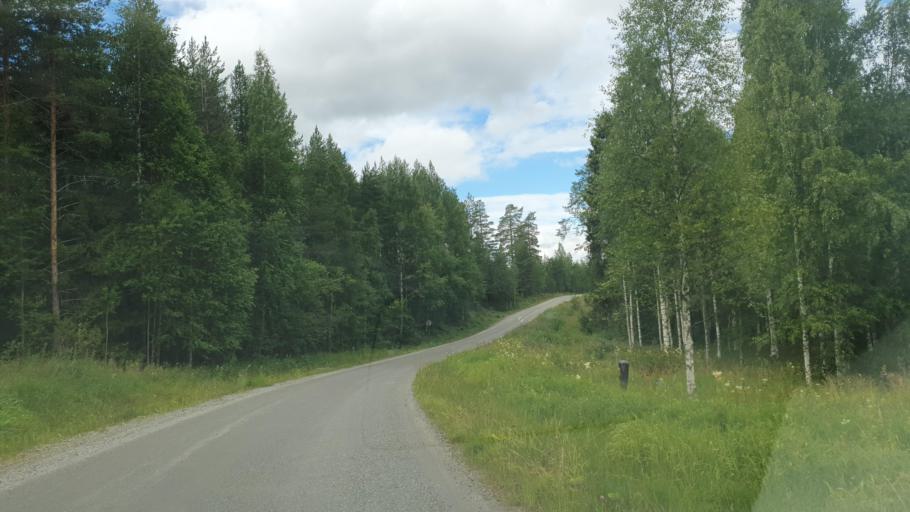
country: FI
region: Kainuu
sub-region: Kehys-Kainuu
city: Kuhmo
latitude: 64.0949
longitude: 29.4181
